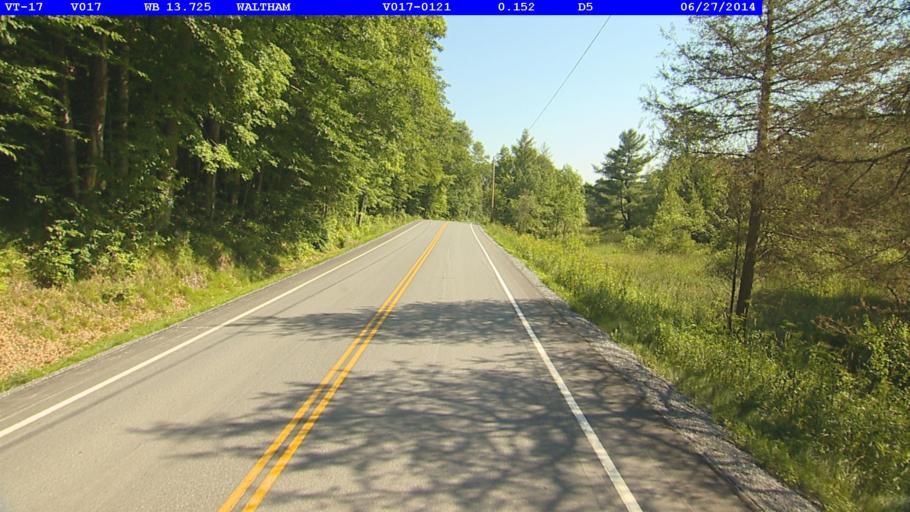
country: US
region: Vermont
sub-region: Addison County
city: Vergennes
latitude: 44.1108
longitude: -73.2181
